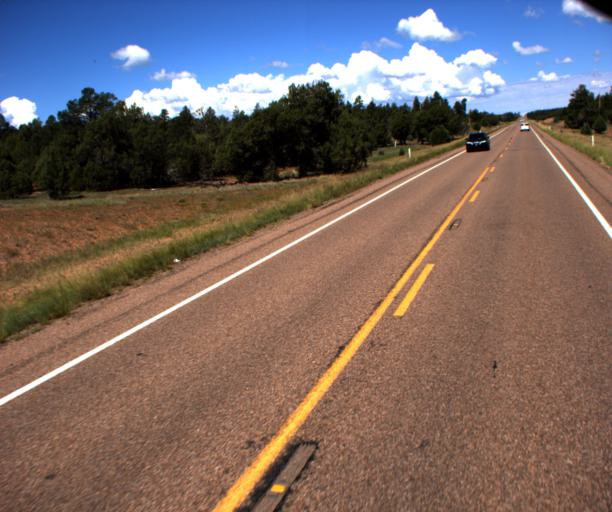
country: US
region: Arizona
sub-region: Navajo County
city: Linden
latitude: 34.3201
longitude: -110.2503
